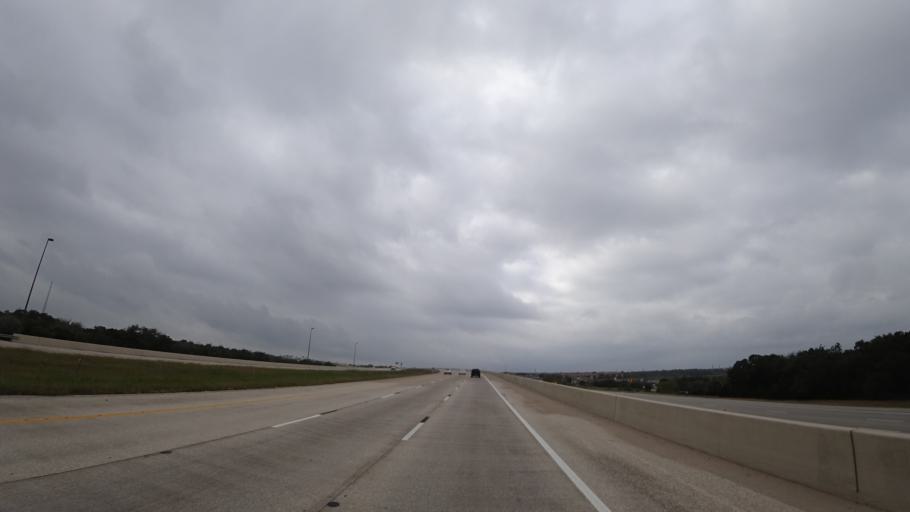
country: US
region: Texas
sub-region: Williamson County
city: Cedar Park
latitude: 30.4901
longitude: -97.8036
